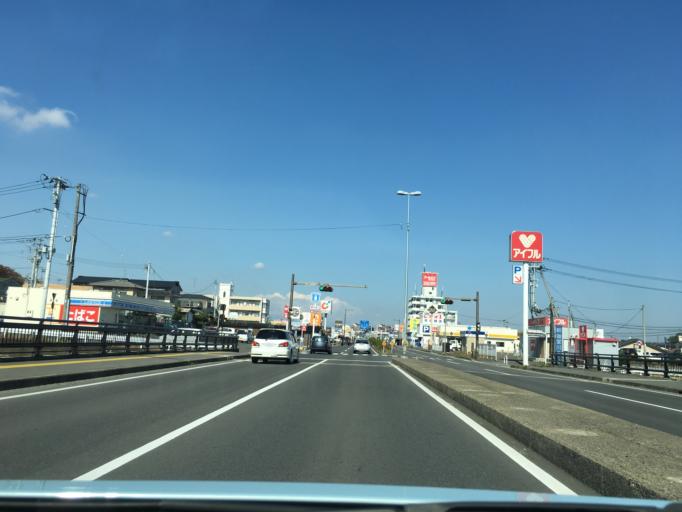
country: JP
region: Fukushima
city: Sukagawa
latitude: 37.2964
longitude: 140.3677
